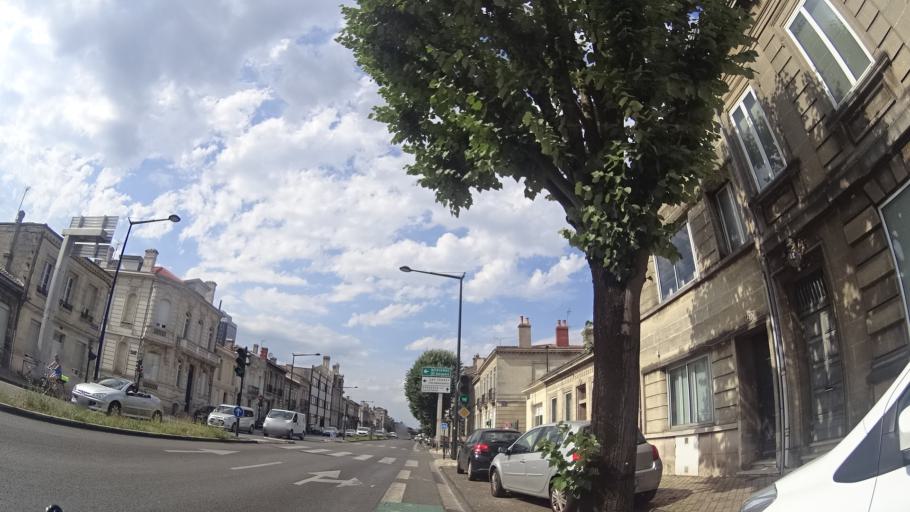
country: FR
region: Aquitaine
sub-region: Departement de la Gironde
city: Bordeaux
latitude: 44.8382
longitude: -0.5990
